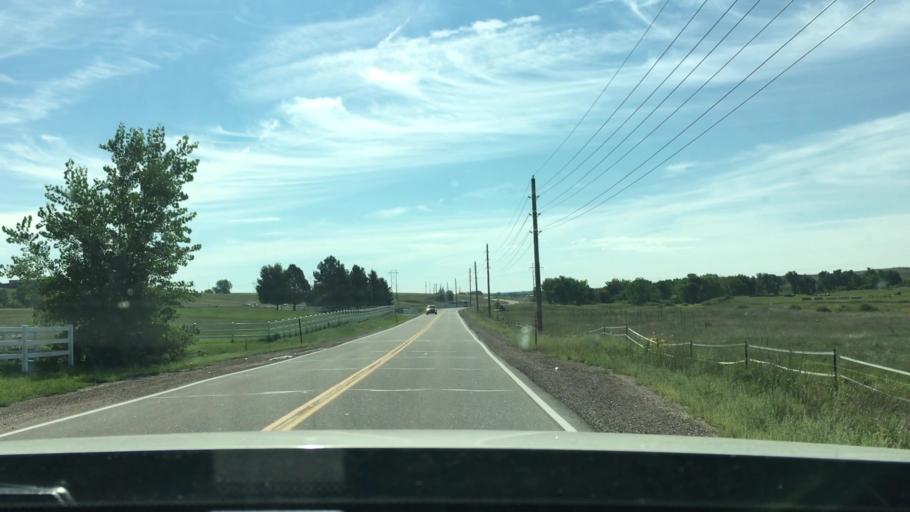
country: US
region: Colorado
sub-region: Douglas County
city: The Pinery
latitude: 39.4317
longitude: -104.7482
